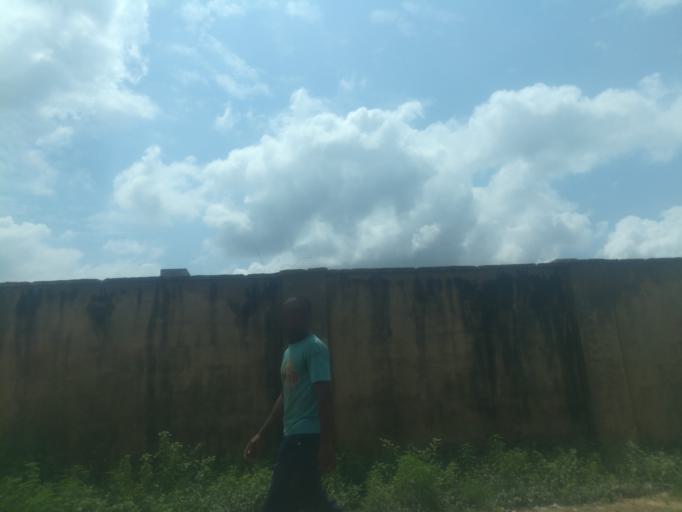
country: NG
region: Oyo
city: Ibadan
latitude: 7.3567
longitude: 3.8432
